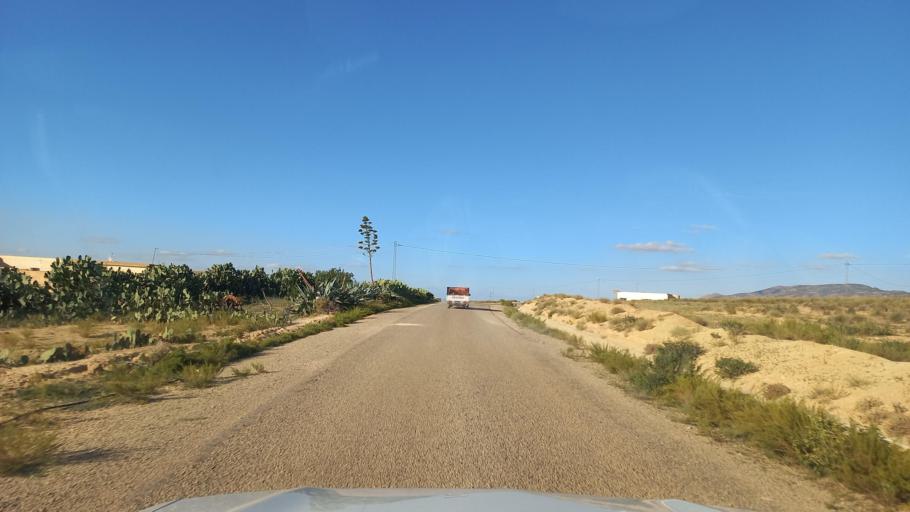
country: TN
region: Al Qasrayn
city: Sbiba
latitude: 35.3546
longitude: 9.1369
